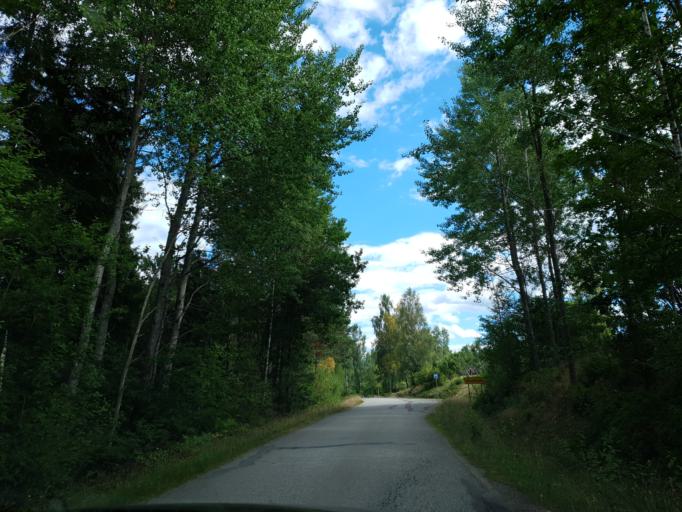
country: SE
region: Kalmar
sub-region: Emmaboda Kommun
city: Emmaboda
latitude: 56.6250
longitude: 15.6450
